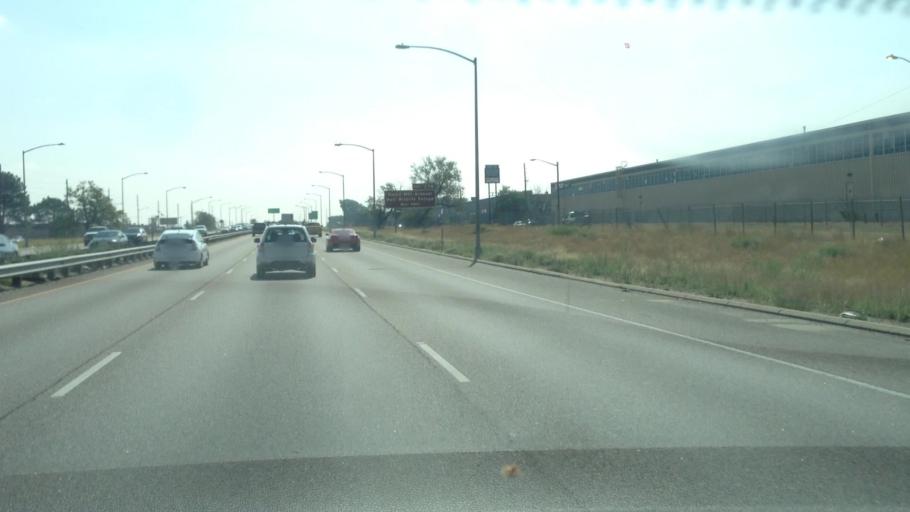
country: US
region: Colorado
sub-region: Adams County
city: Commerce City
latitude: 39.7781
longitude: -104.9200
